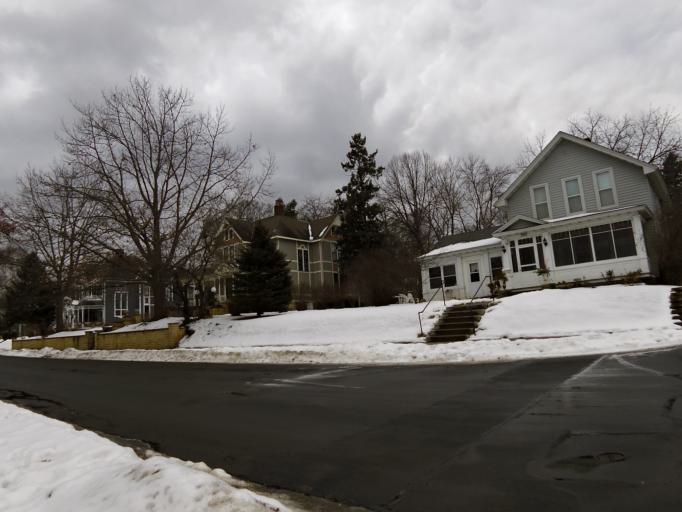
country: US
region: Minnesota
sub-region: Washington County
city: Stillwater
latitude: 45.0535
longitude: -92.8120
